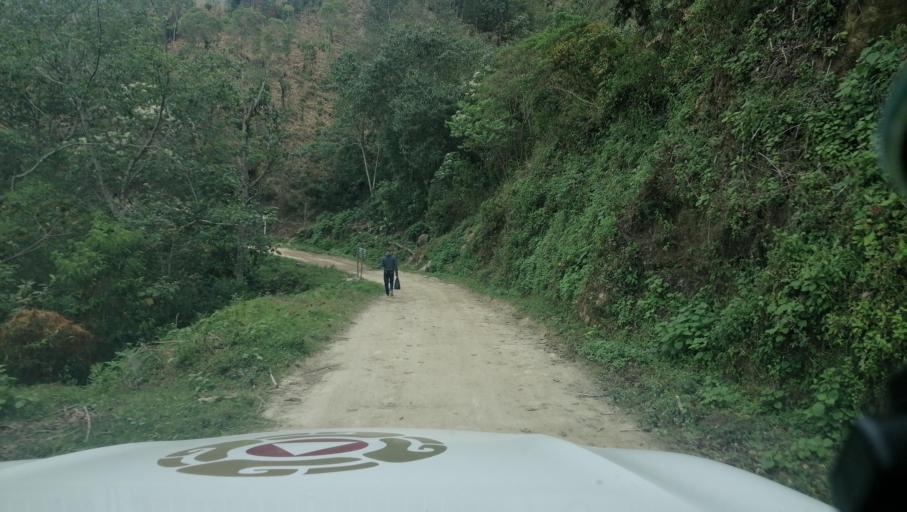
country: GT
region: San Marcos
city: Tacana
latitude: 15.2065
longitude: -92.1696
